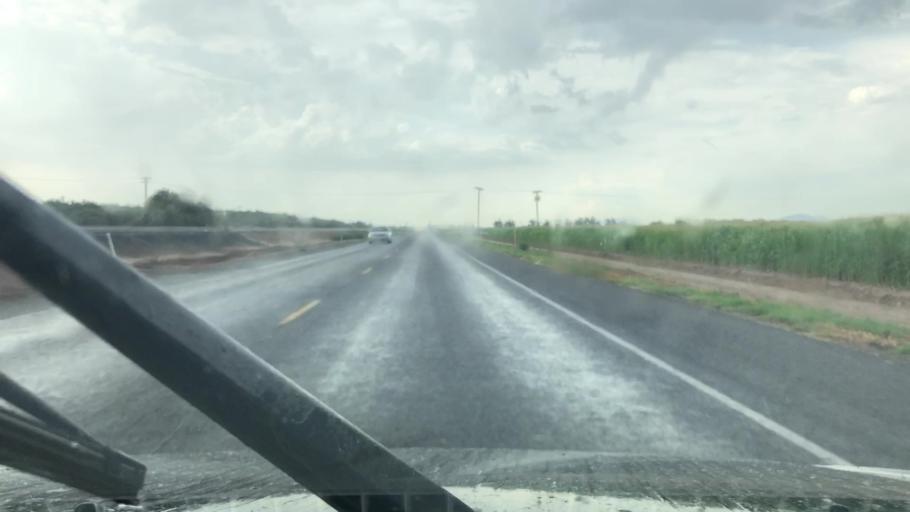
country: US
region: New Mexico
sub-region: Dona Ana County
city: Mesquite
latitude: 32.1447
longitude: -106.6840
